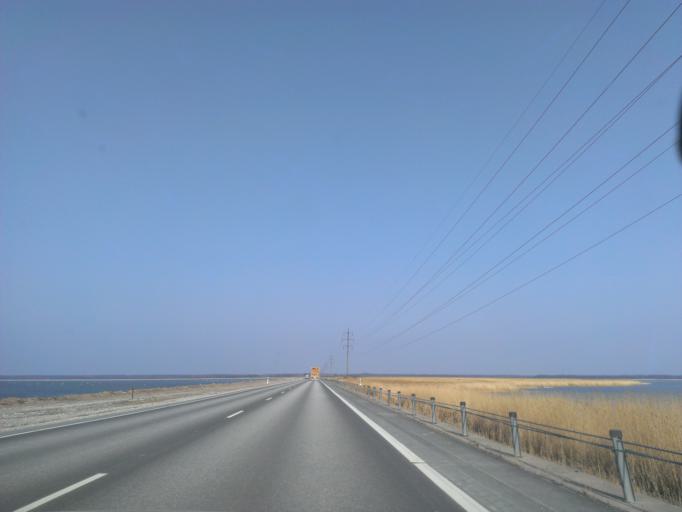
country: EE
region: Saare
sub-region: Orissaare vald
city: Orissaare
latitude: 58.5531
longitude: 23.1425
